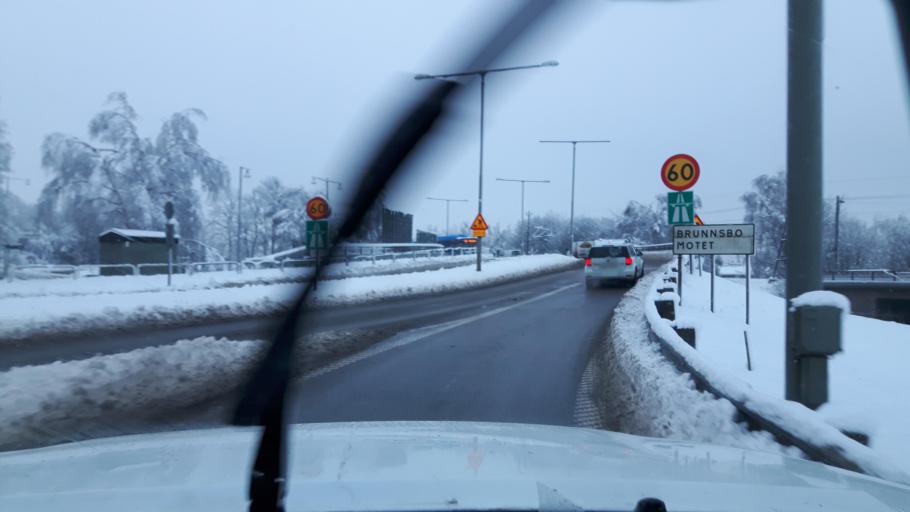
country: SE
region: Vaestra Goetaland
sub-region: Goteborg
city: Goeteborg
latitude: 57.7269
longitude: 11.9691
